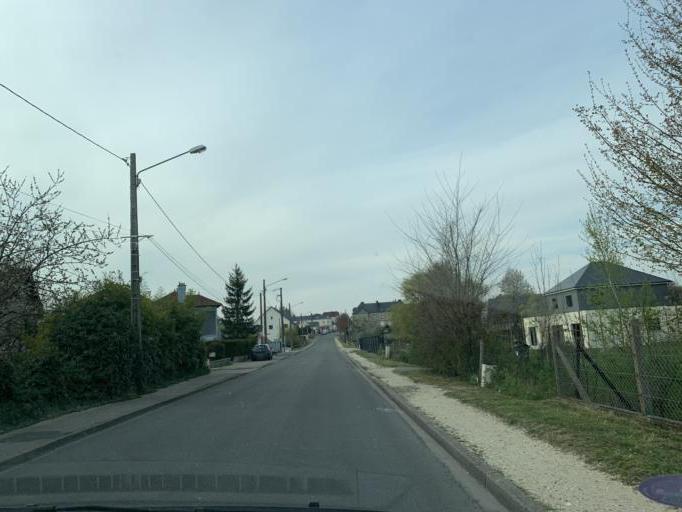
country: FR
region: Haute-Normandie
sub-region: Departement de la Seine-Maritime
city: La Mailleraye-sur-Seine
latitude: 49.4795
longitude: 0.7737
